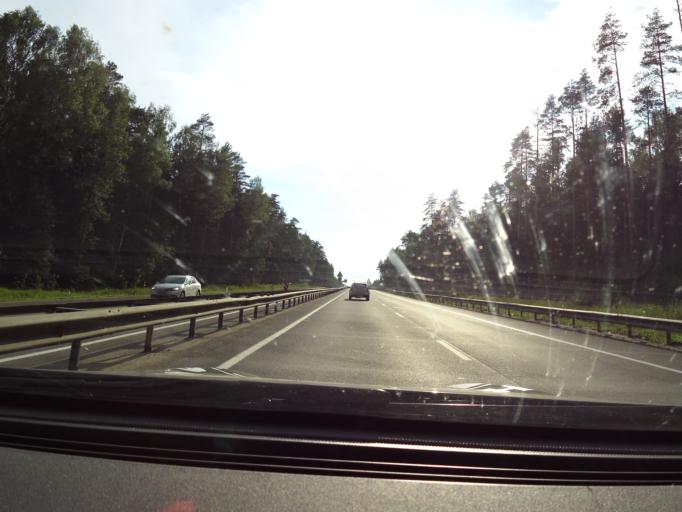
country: RU
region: Vladimir
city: Stepantsevo
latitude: 56.2283
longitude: 41.6866
